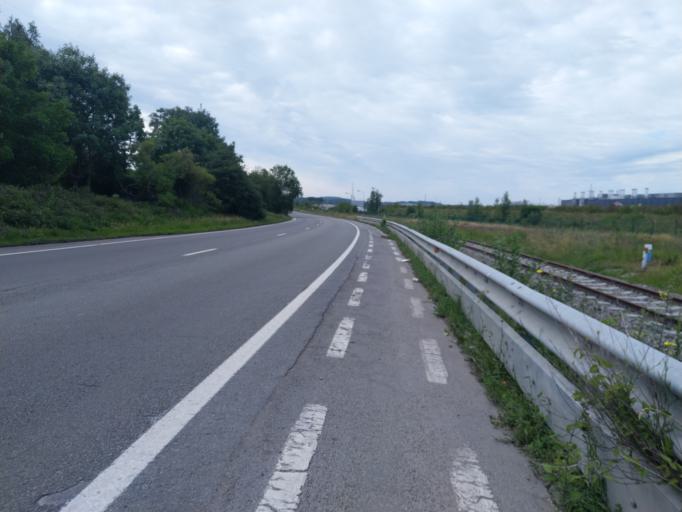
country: BE
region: Wallonia
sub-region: Province du Hainaut
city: Quaregnon
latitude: 50.4682
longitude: 3.8686
